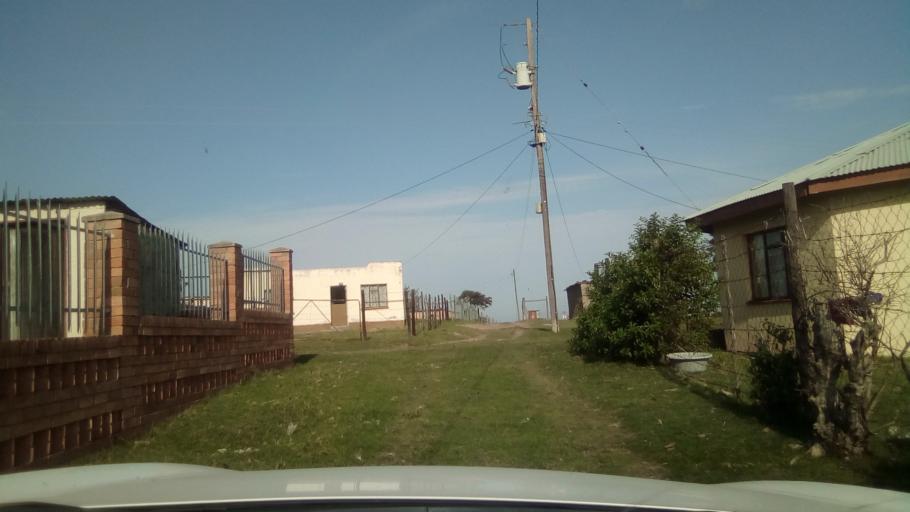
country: ZA
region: Eastern Cape
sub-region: Buffalo City Metropolitan Municipality
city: Bhisho
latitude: -32.9875
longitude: 27.2707
